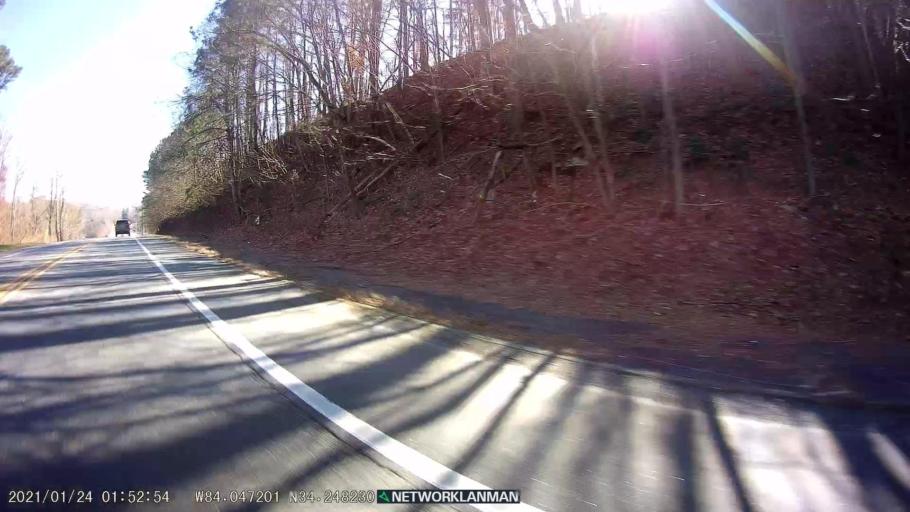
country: US
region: Georgia
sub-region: Forsyth County
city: Cumming
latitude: 34.2482
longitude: -84.0470
